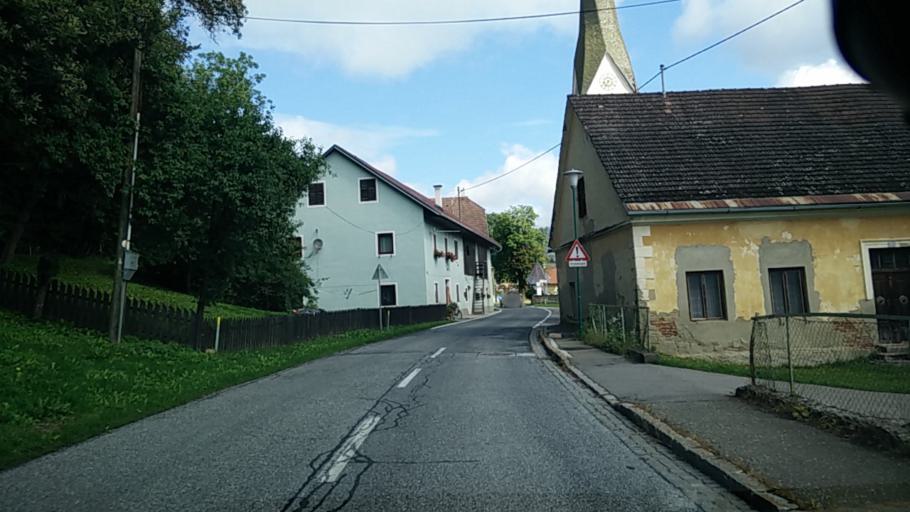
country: AT
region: Carinthia
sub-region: Politischer Bezirk Volkermarkt
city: Voelkermarkt
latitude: 46.6752
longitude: 14.5725
